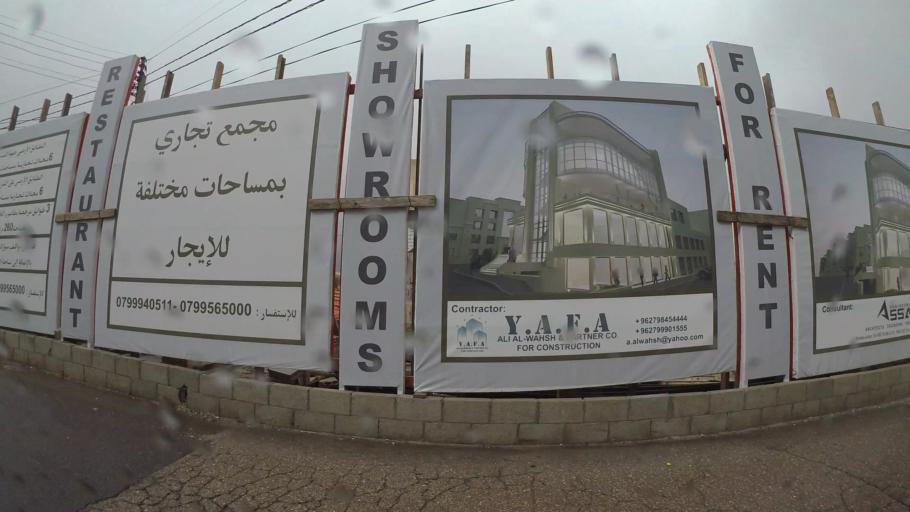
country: JO
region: Amman
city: Wadi as Sir
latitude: 31.9750
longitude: 35.8515
